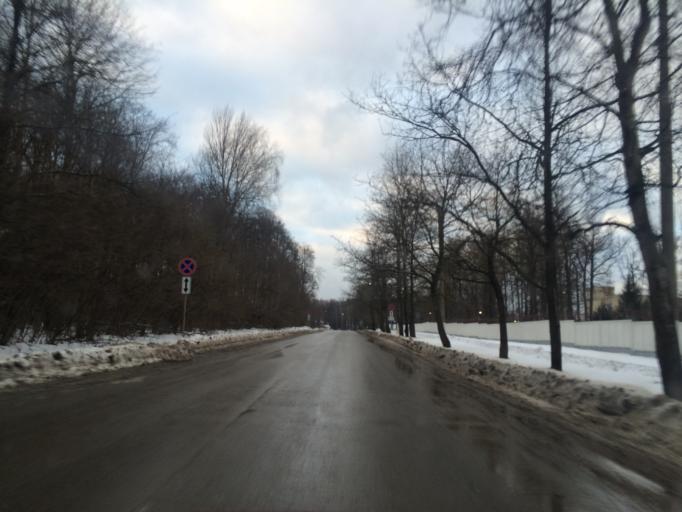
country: RU
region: Tula
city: Tula
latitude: 54.2172
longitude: 37.7105
